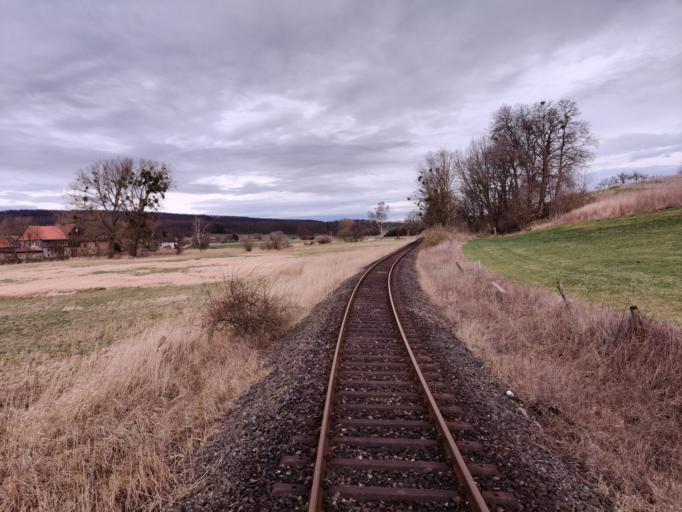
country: DE
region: Lower Saxony
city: Bockenem
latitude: 52.0360
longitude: 10.1213
